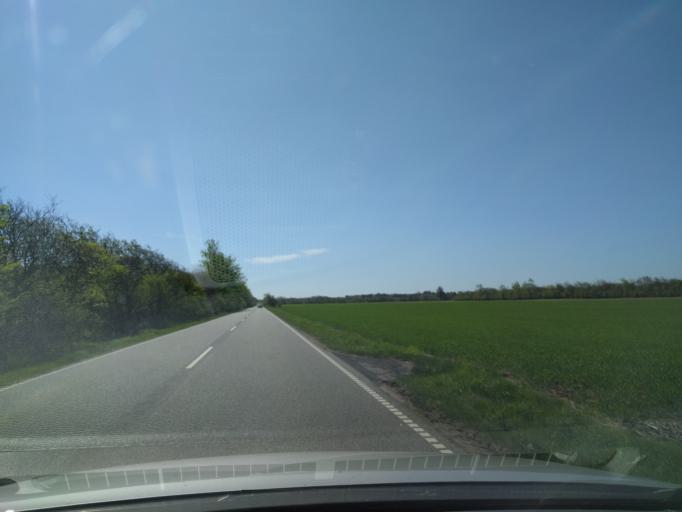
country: DK
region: Central Jutland
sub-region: Ringkobing-Skjern Kommune
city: Tarm
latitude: 55.8822
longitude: 8.5262
